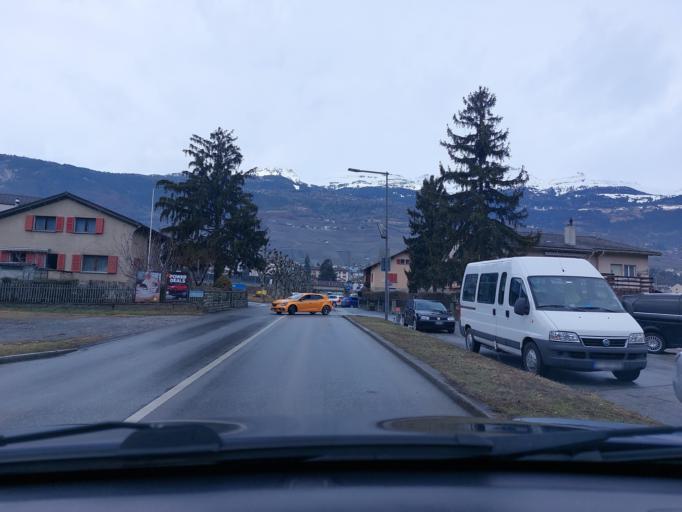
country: CH
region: Valais
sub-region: Sierre District
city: Sierre
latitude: 46.2849
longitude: 7.5271
